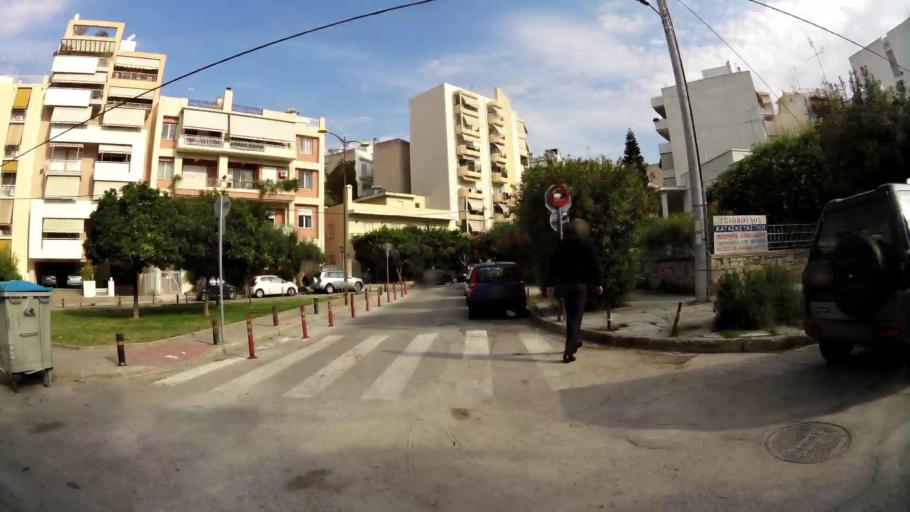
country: GR
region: Attica
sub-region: Nomarchia Athinas
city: Kallithea
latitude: 37.9435
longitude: 23.7027
